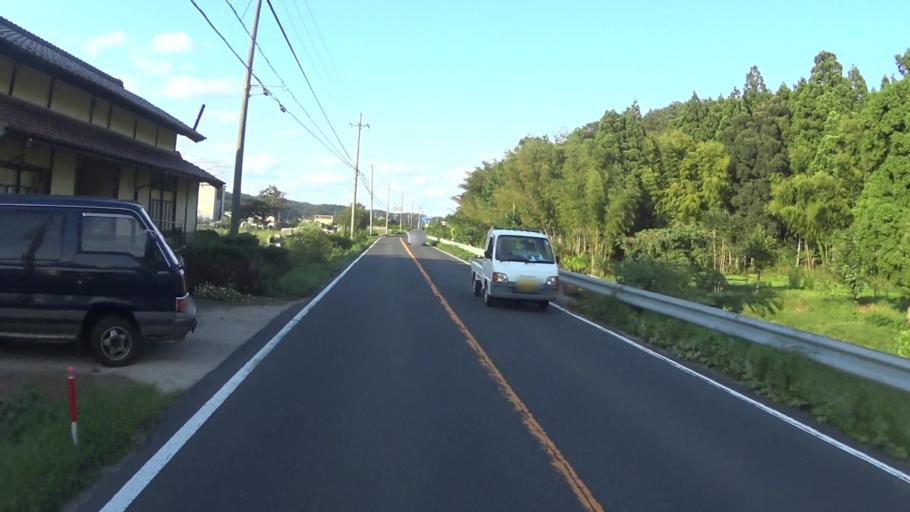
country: JP
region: Kyoto
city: Miyazu
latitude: 35.5953
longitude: 135.0437
